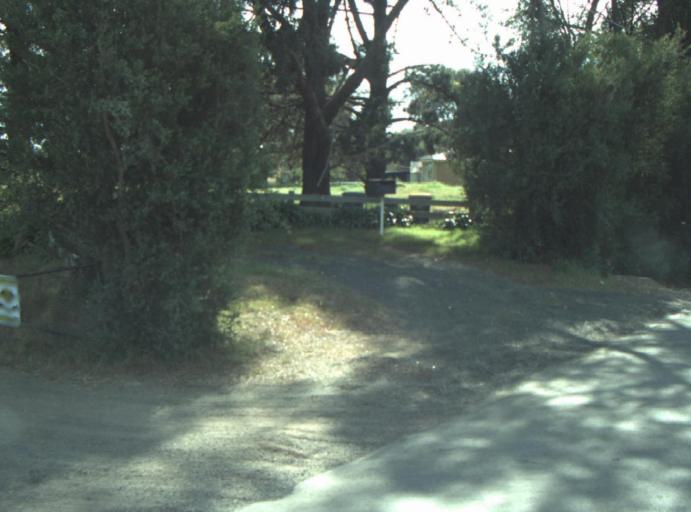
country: AU
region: Victoria
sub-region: Greater Geelong
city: Clifton Springs
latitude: -38.1842
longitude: 144.5407
